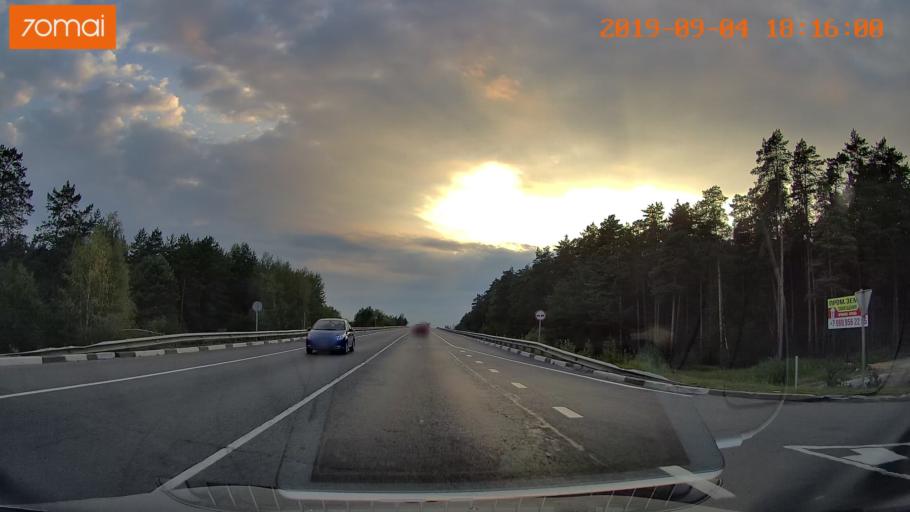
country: RU
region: Moskovskaya
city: Lopatinskiy
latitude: 55.3442
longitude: 38.6924
